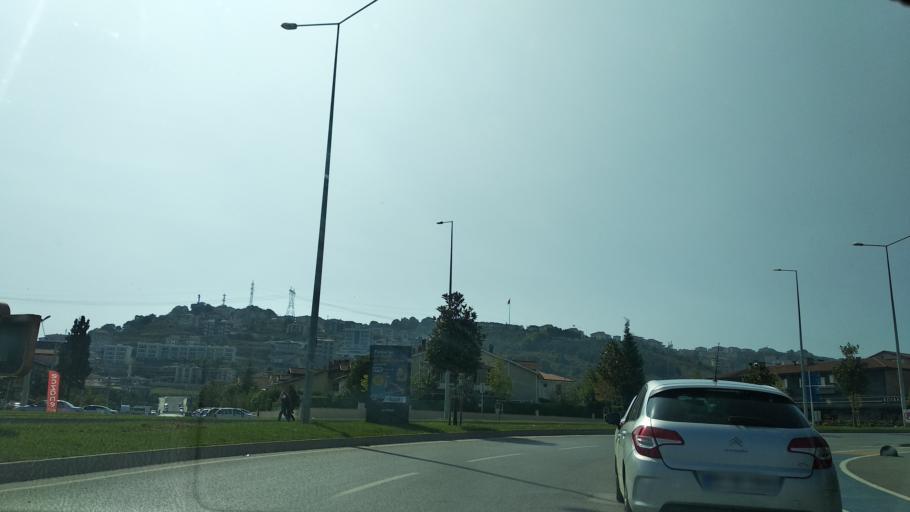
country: TR
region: Sakarya
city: Adapazari
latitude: 40.7602
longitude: 30.3627
